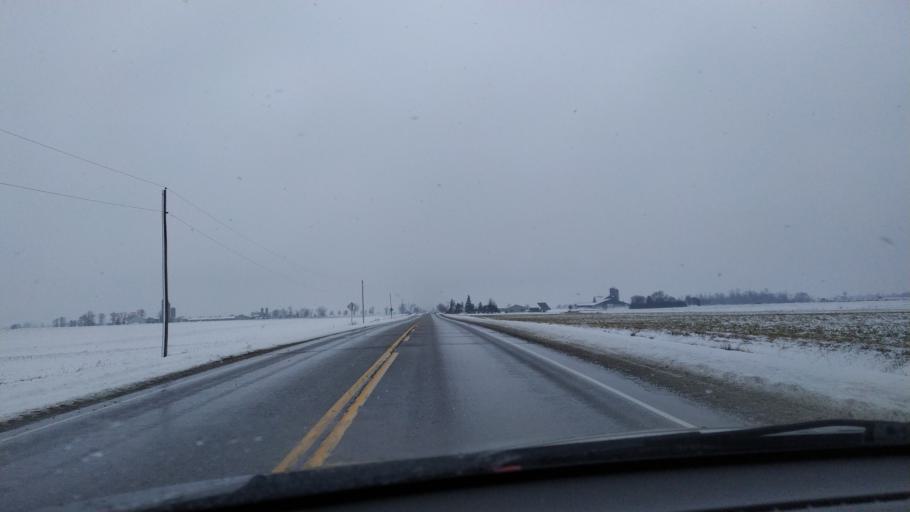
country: CA
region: Ontario
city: Stratford
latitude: 43.5365
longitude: -80.8668
